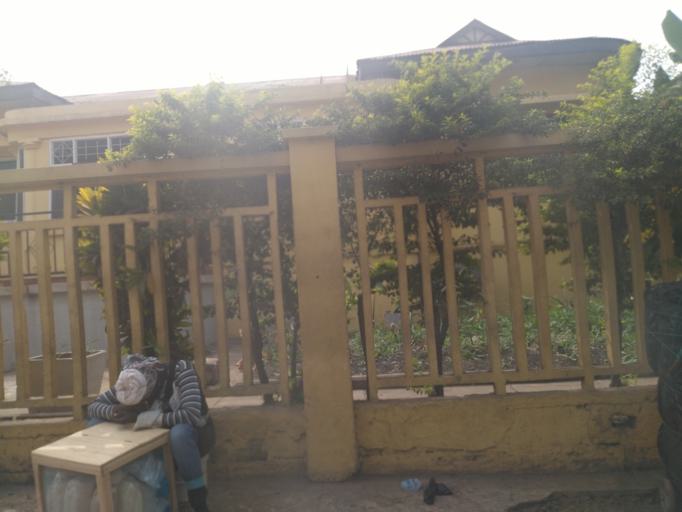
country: GH
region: Ashanti
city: Kumasi
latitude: 6.7030
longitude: -1.6245
